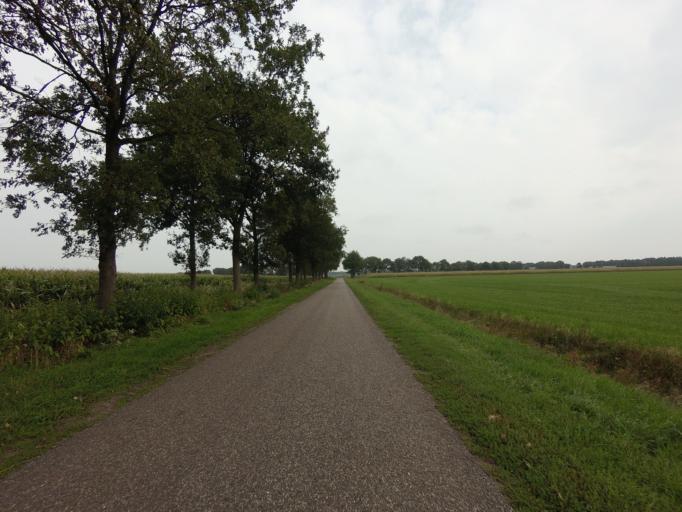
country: NL
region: Drenthe
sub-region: Gemeente Westerveld
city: Dwingeloo
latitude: 52.8739
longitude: 6.4576
